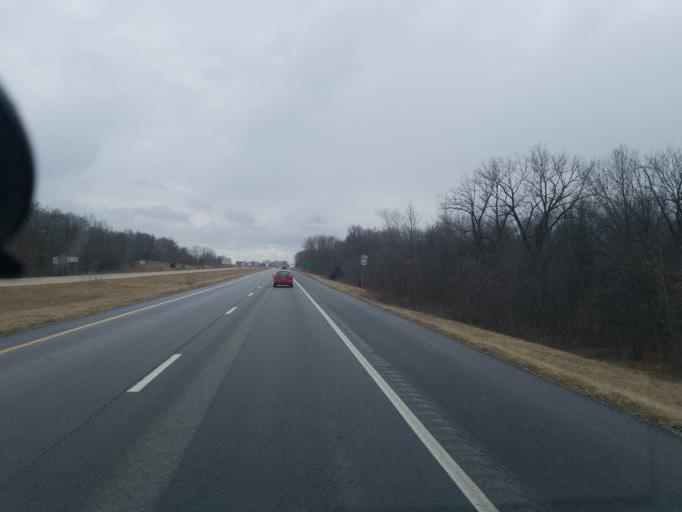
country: US
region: Missouri
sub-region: Randolph County
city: Moberly
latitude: 39.3876
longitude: -92.4134
